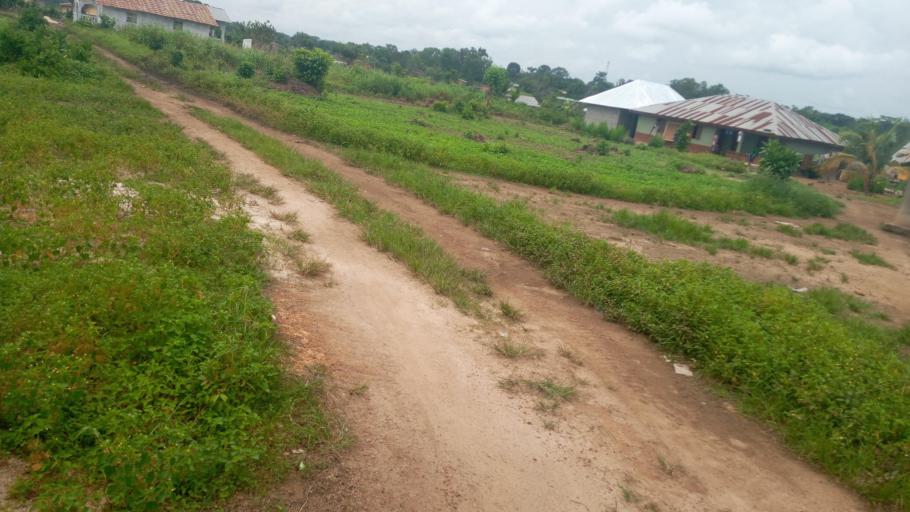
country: SL
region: Southern Province
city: Mogbwemo
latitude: 7.7742
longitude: -12.3014
